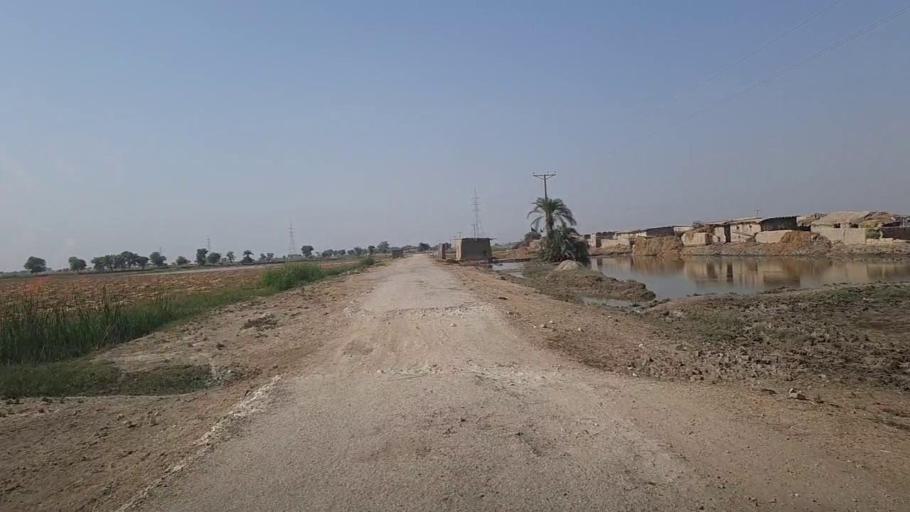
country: PK
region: Sindh
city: Kandhkot
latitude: 28.4087
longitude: 69.2484
